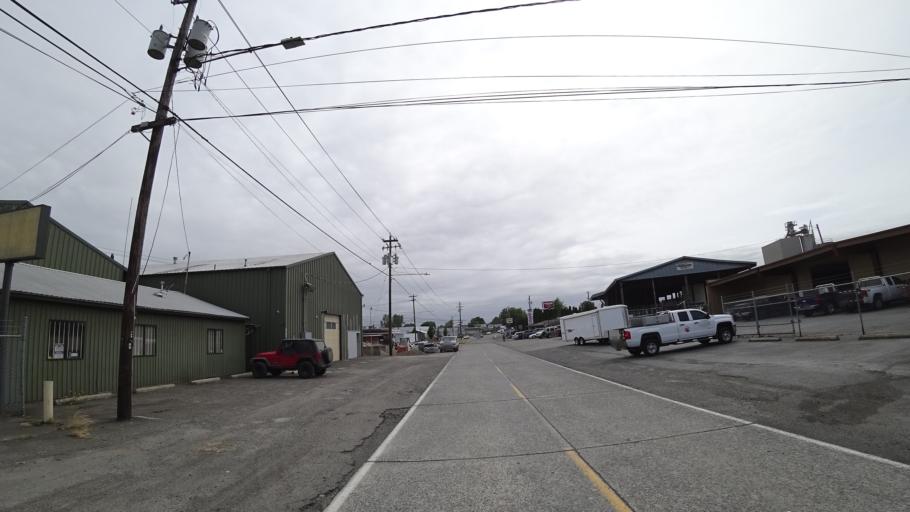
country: US
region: Oregon
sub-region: Multnomah County
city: Portland
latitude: 45.5772
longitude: -122.6490
